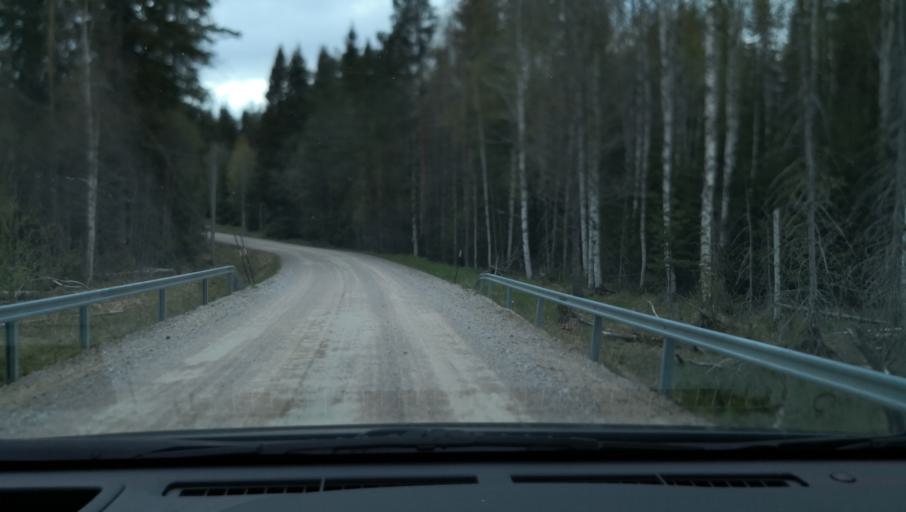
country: SE
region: Vaestmanland
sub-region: Fagersta Kommun
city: Fagersta
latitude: 60.0918
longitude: 15.8123
